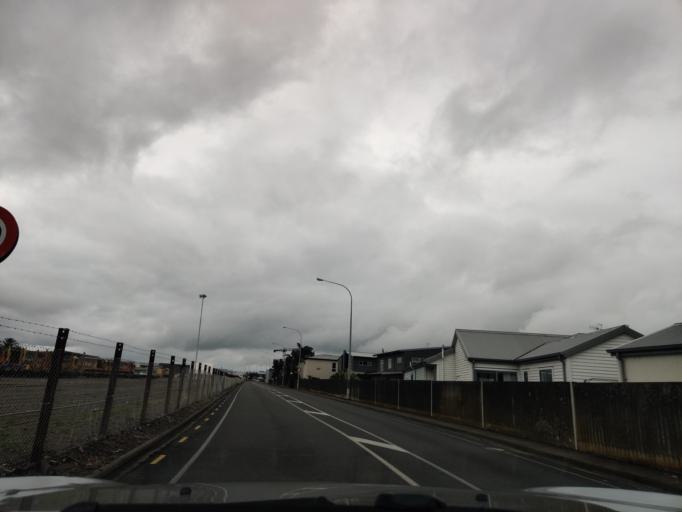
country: NZ
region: Hawke's Bay
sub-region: Napier City
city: Napier
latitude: -39.4802
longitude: 176.9017
